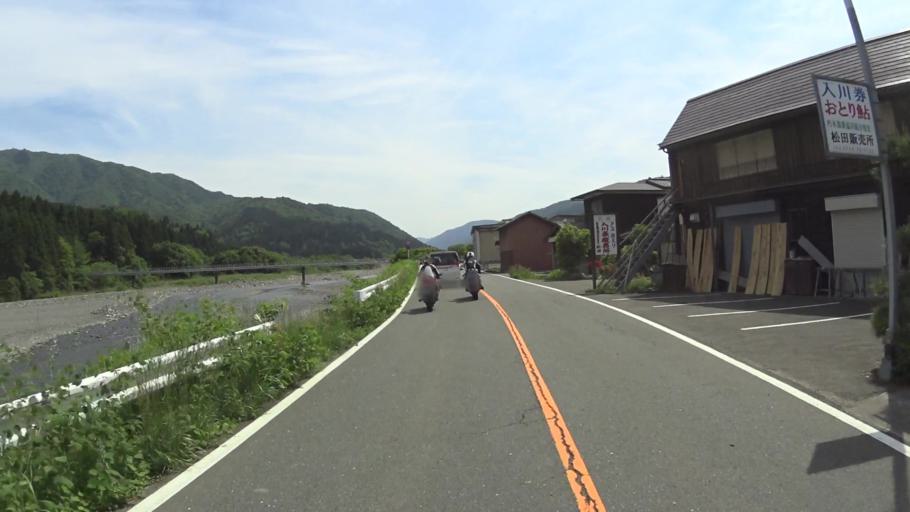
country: JP
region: Shiga Prefecture
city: Kitahama
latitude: 35.3475
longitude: 135.9122
